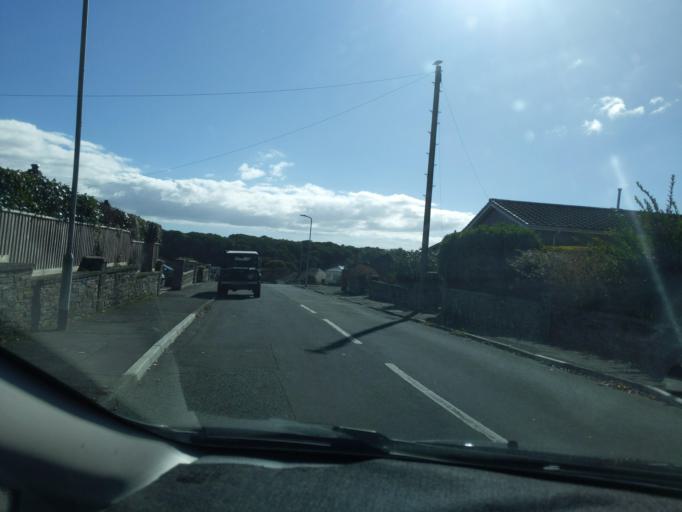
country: GB
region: England
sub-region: Plymouth
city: Plymstock
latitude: 50.3576
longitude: -4.0768
